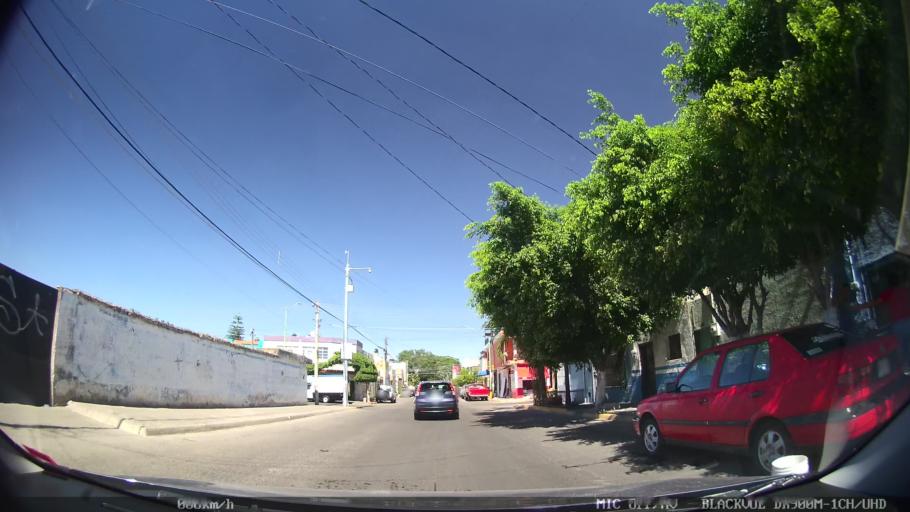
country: MX
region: Jalisco
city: Tlaquepaque
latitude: 20.6525
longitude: -103.2934
